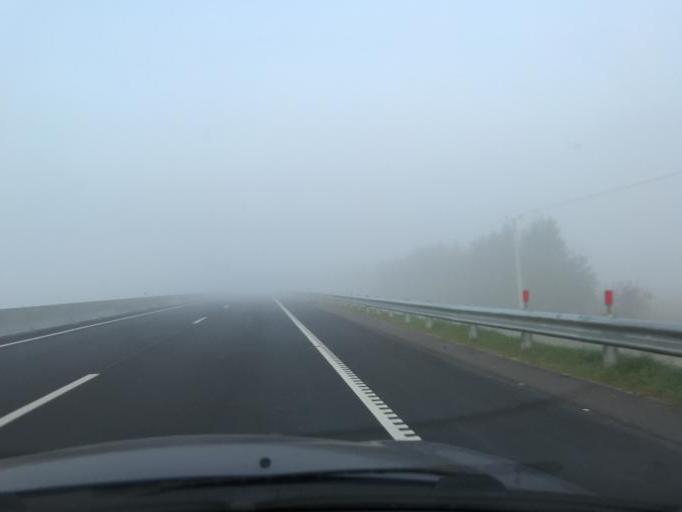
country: BY
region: Minsk
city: Ivyanyets
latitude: 54.0421
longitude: 26.6988
